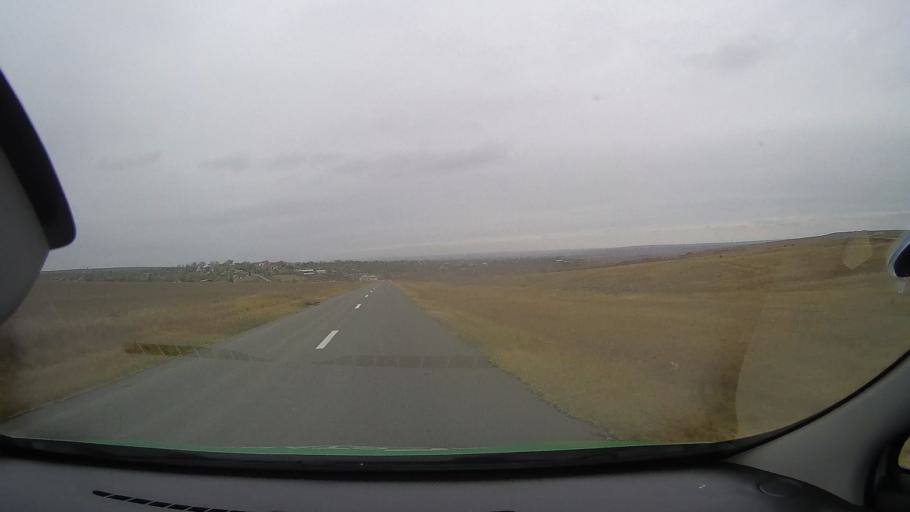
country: RO
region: Constanta
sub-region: Comuna Pantelimon
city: Pantelimon
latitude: 44.5369
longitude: 28.3275
